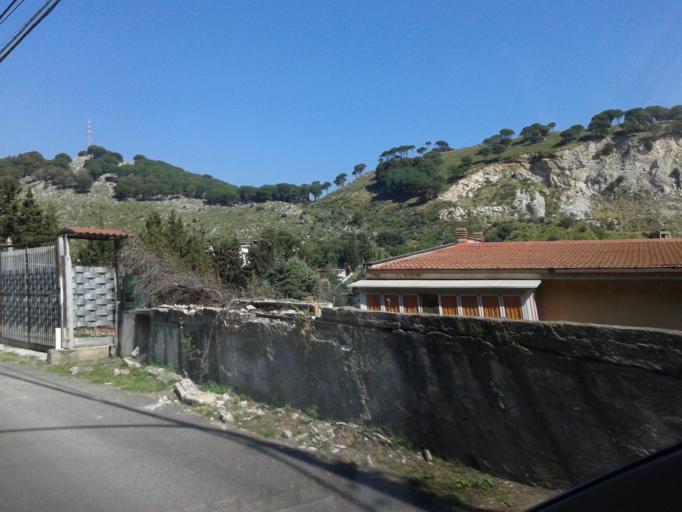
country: IT
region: Sicily
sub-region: Palermo
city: Piano dei Geli
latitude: 38.1162
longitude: 13.2896
